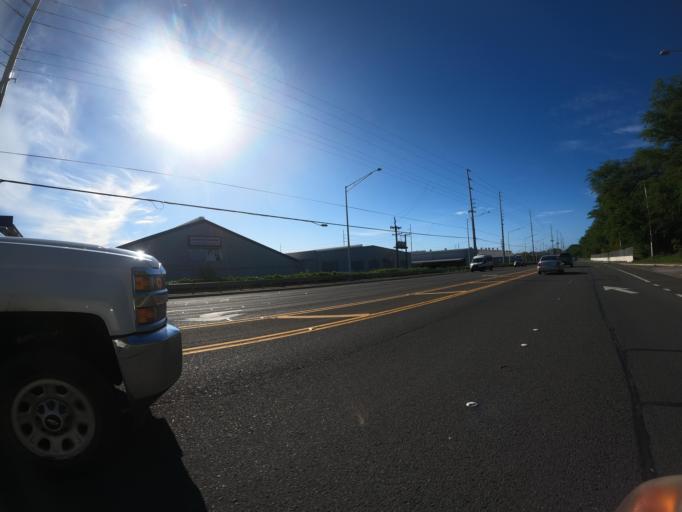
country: US
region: Hawaii
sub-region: Honolulu County
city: Halawa Heights
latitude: 21.3444
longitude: -157.8995
